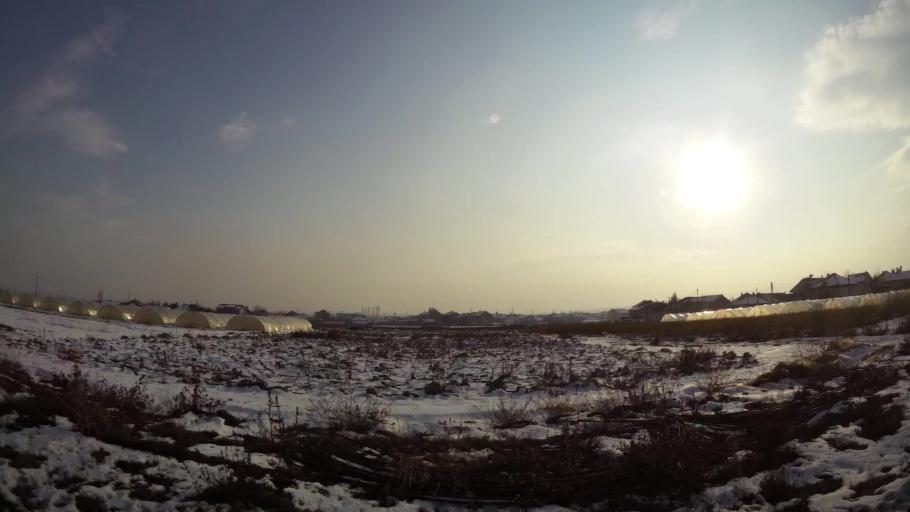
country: MK
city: Creshevo
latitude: 42.0336
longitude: 21.5213
